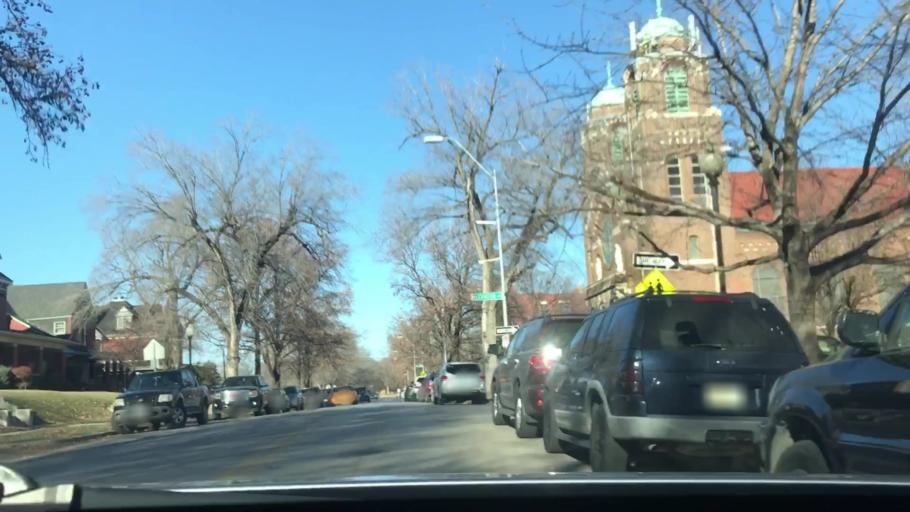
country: US
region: Missouri
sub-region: Clay County
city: North Kansas City
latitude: 39.1104
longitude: -94.5444
